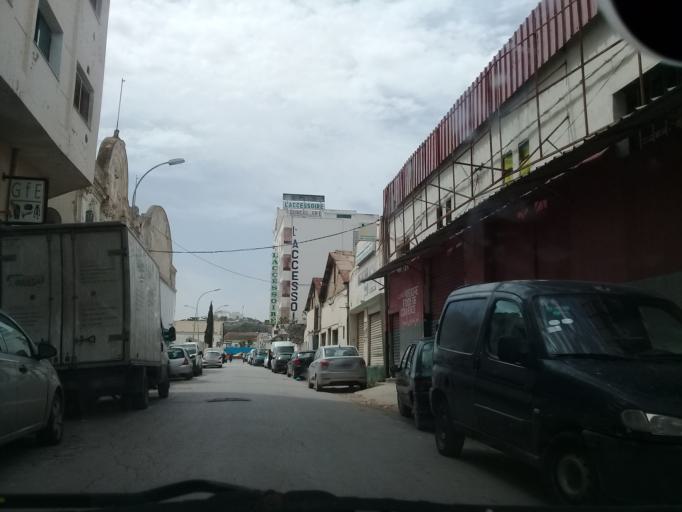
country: TN
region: Tunis
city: Tunis
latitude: 36.7920
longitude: 10.1836
